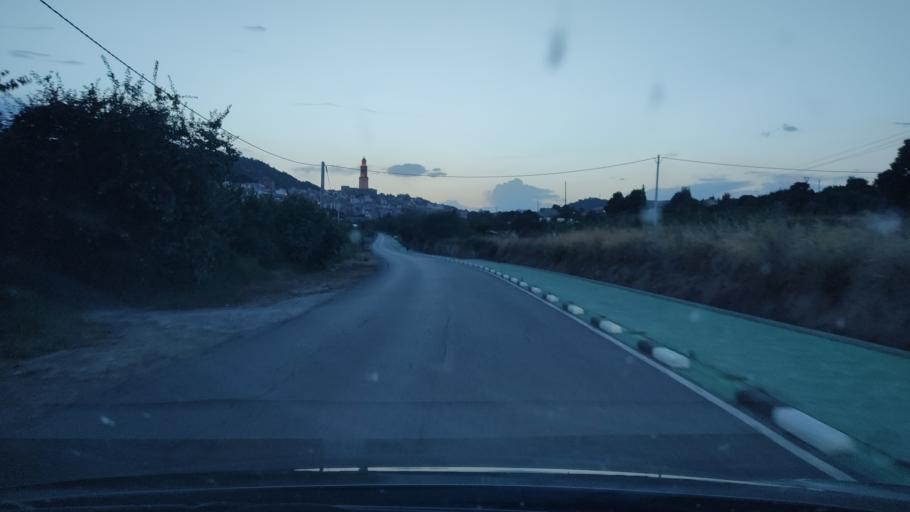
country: ES
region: Valencia
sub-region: Provincia de Castello
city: Jerica
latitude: 39.9086
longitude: -0.5612
